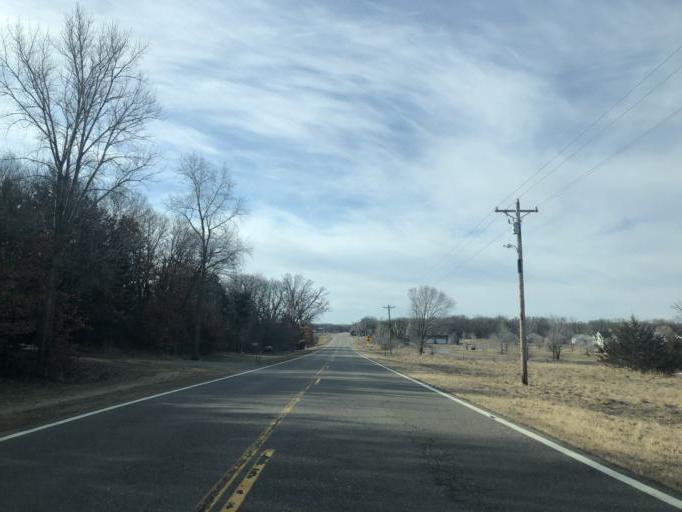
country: US
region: Minnesota
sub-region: Sherburne County
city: Becker
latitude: 45.4047
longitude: -93.8498
